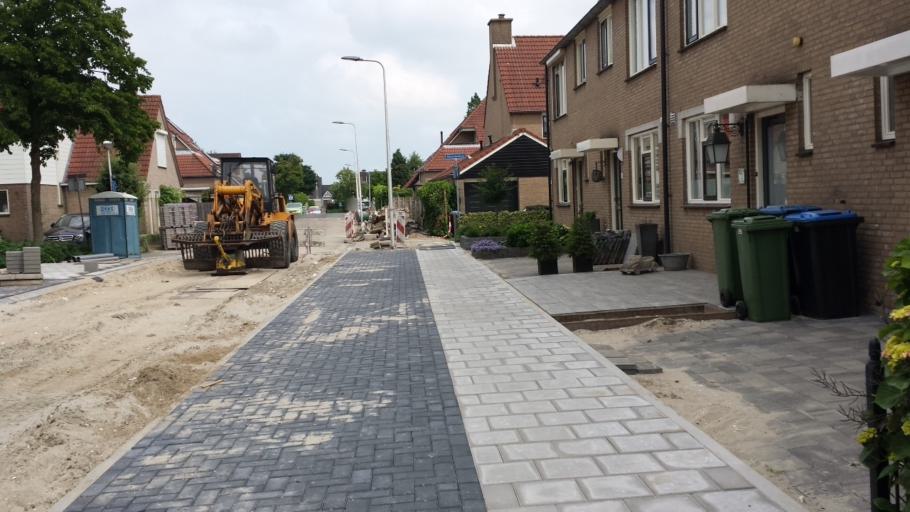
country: NL
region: South Holland
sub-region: Bodegraven-Reeuwijk
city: Reeuwijk
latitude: 52.0503
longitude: 4.7299
